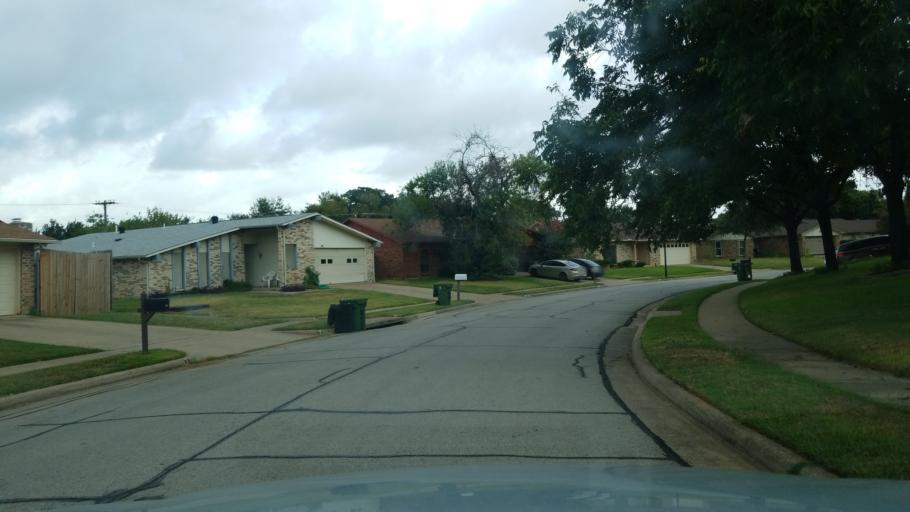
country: US
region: Texas
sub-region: Tarrant County
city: Euless
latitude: 32.8458
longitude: -97.1095
